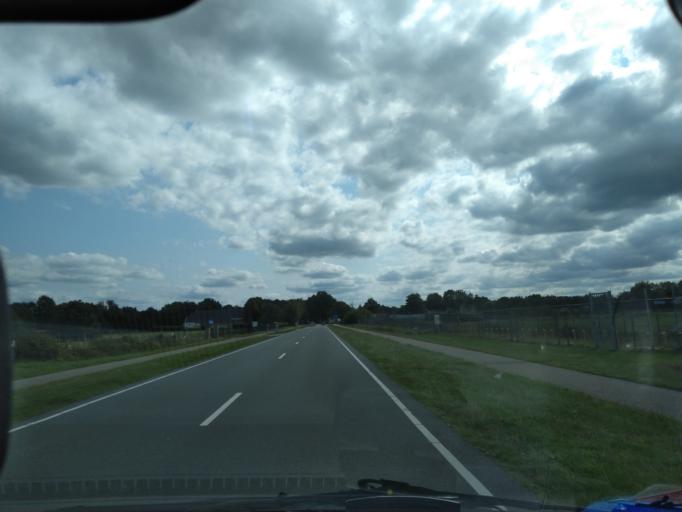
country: NL
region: Groningen
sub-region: Gemeente Haren
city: Haren
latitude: 53.1270
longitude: 6.5938
